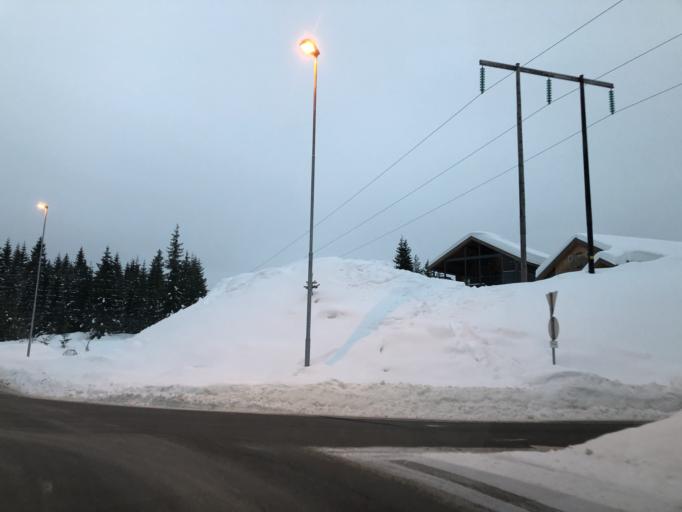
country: NO
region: Hedmark
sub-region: Trysil
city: Innbygda
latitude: 61.3043
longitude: 12.2472
